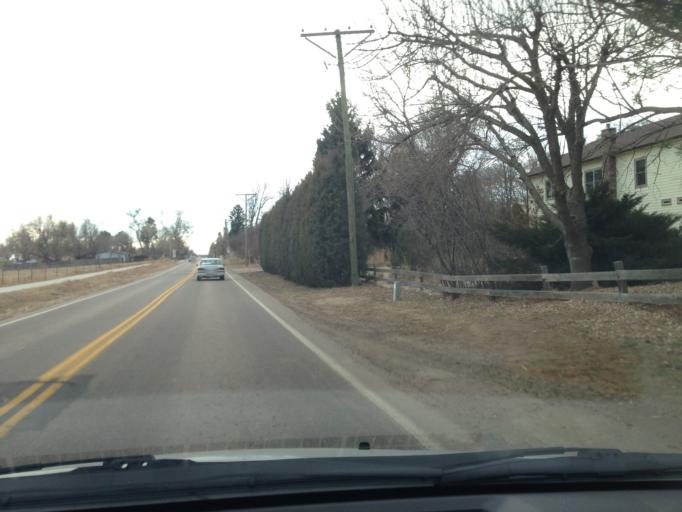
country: US
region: Colorado
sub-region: Weld County
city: Windsor
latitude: 40.5352
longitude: -104.9823
